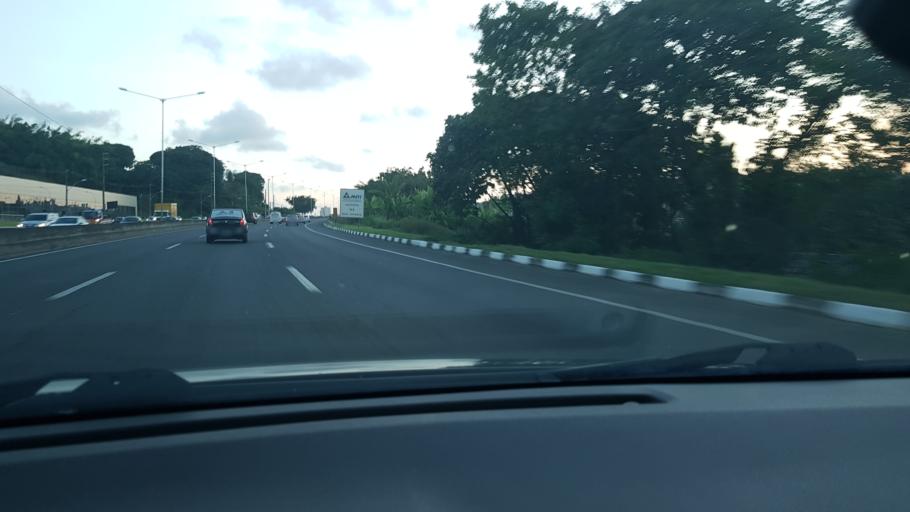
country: BR
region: Bahia
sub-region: Salvador
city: Salvador
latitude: -12.9585
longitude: -38.4728
